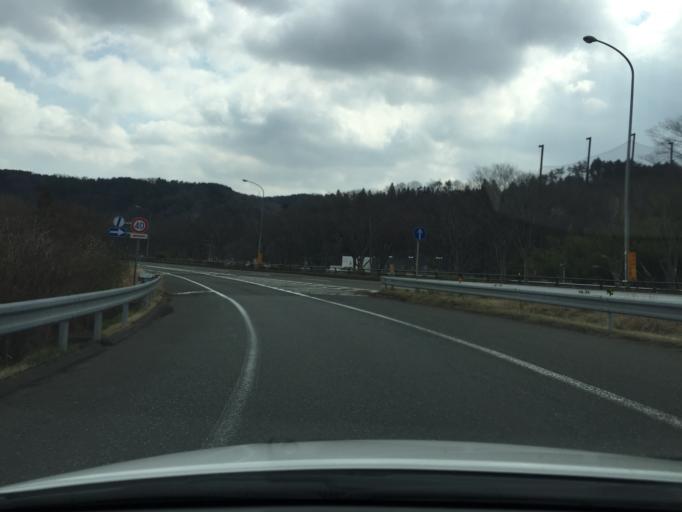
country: JP
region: Miyagi
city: Sendai
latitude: 38.2600
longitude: 140.8173
